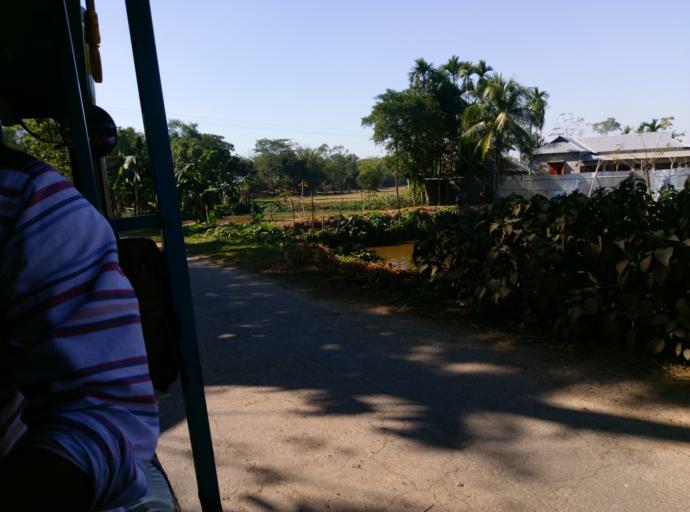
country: BD
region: Dhaka
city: Netrakona
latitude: 25.0696
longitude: 90.5059
